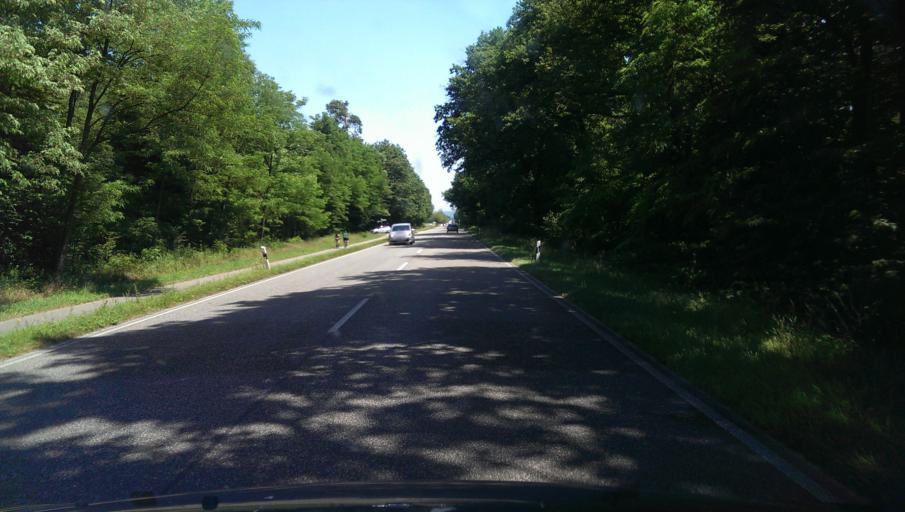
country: DE
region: Baden-Wuerttemberg
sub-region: Karlsruhe Region
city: Muggensturm
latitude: 48.8943
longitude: 8.2920
